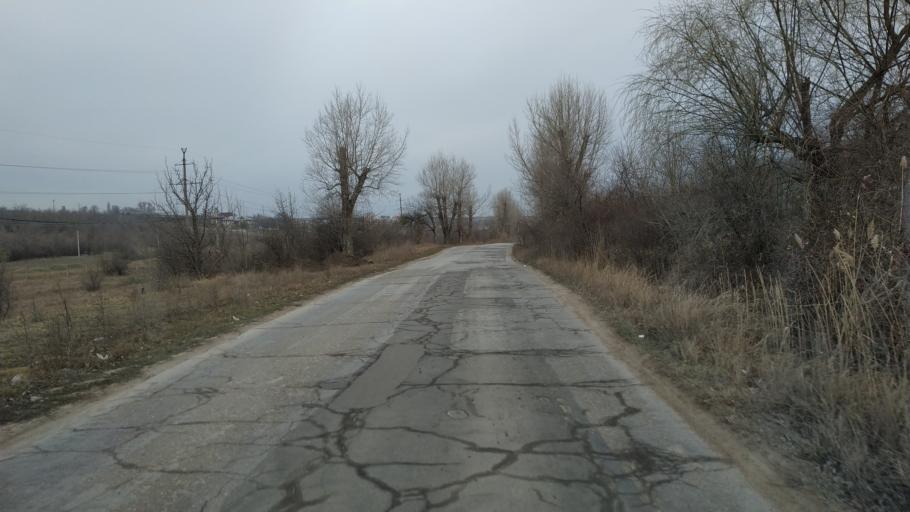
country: MD
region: Chisinau
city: Vatra
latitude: 47.0762
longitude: 28.7703
